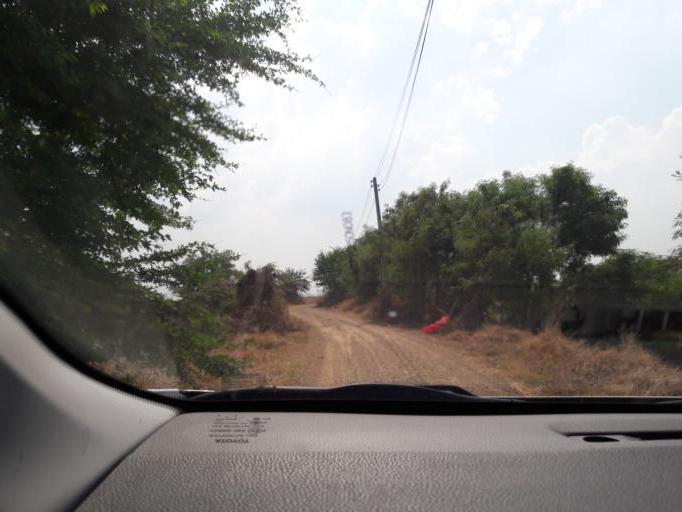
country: TH
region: Ang Thong
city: Ang Thong
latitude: 14.5646
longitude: 100.4095
